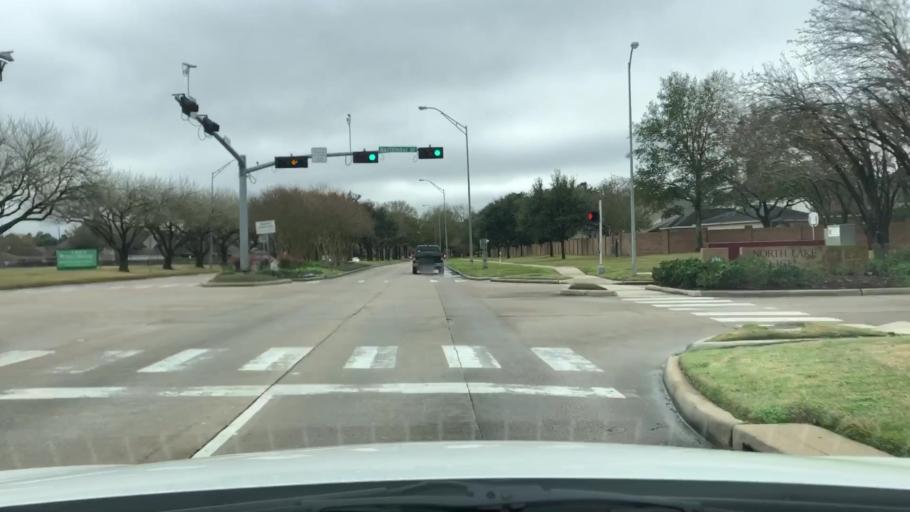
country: US
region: Texas
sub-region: Fort Bend County
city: Cinco Ranch
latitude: 29.7445
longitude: -95.7515
